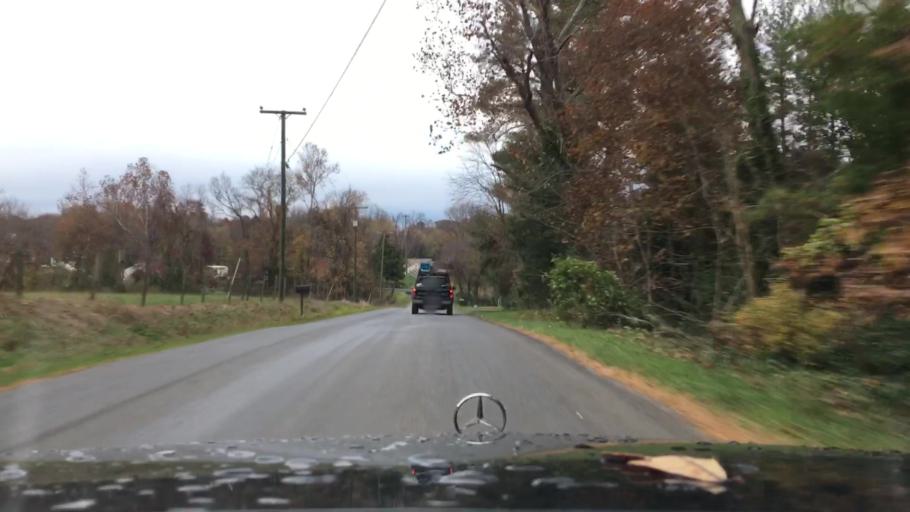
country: US
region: Virginia
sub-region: Campbell County
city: Altavista
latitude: 37.1454
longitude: -79.3037
